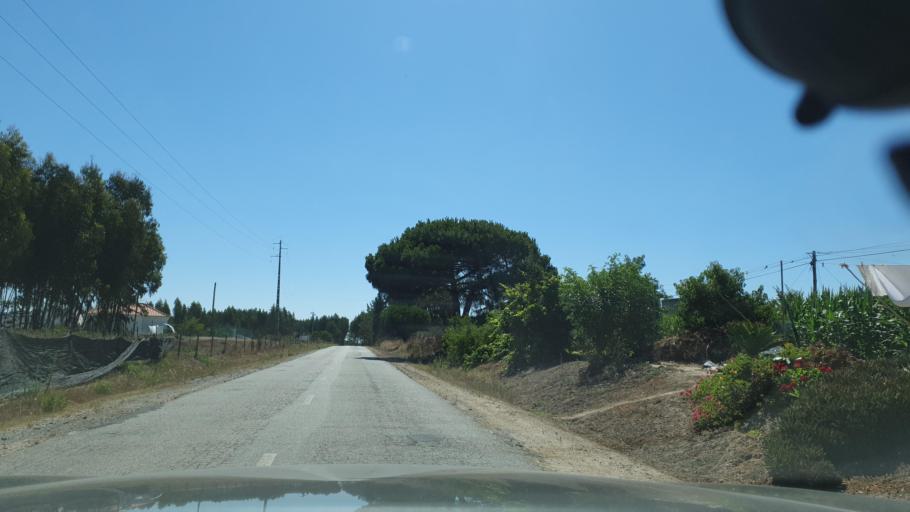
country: PT
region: Beja
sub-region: Odemira
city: Sao Teotonio
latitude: 37.4987
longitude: -8.6688
